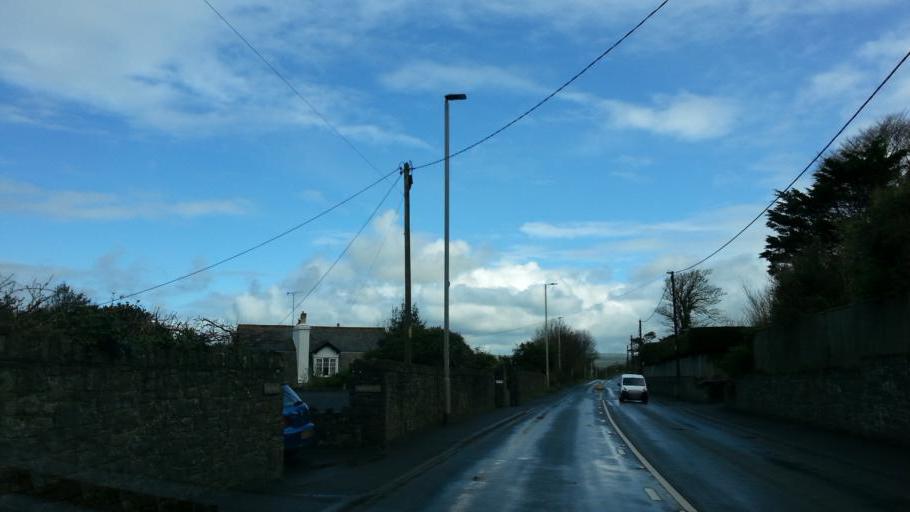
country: GB
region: England
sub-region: Devon
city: Appledore
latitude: 51.0554
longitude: -4.1780
